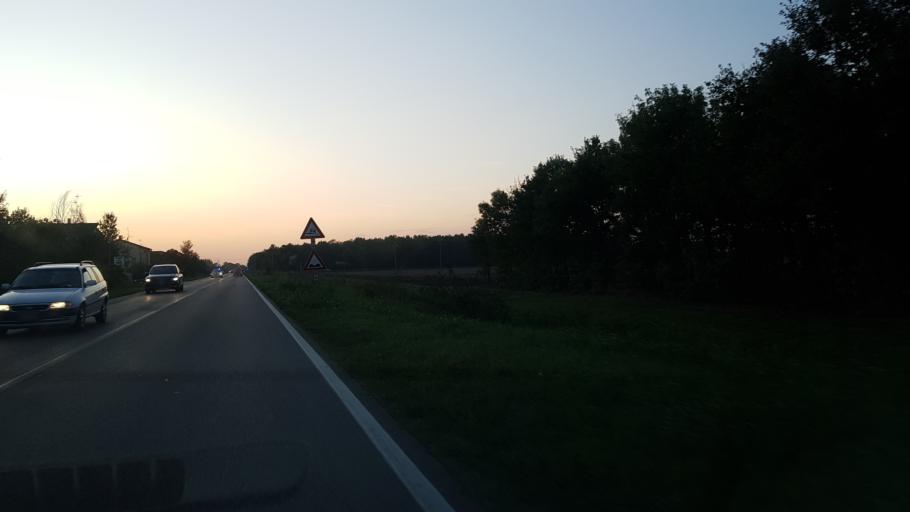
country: IT
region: Emilia-Romagna
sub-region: Provincia di Modena
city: Solara
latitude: 44.8041
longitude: 11.0968
